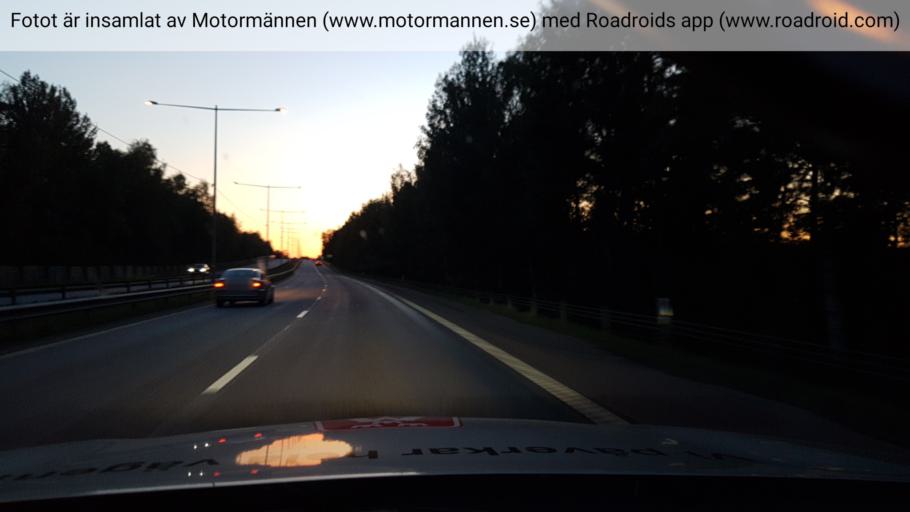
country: SE
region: Vaermland
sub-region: Karlstads Kommun
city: Karlstad
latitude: 59.4019
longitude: 13.5484
